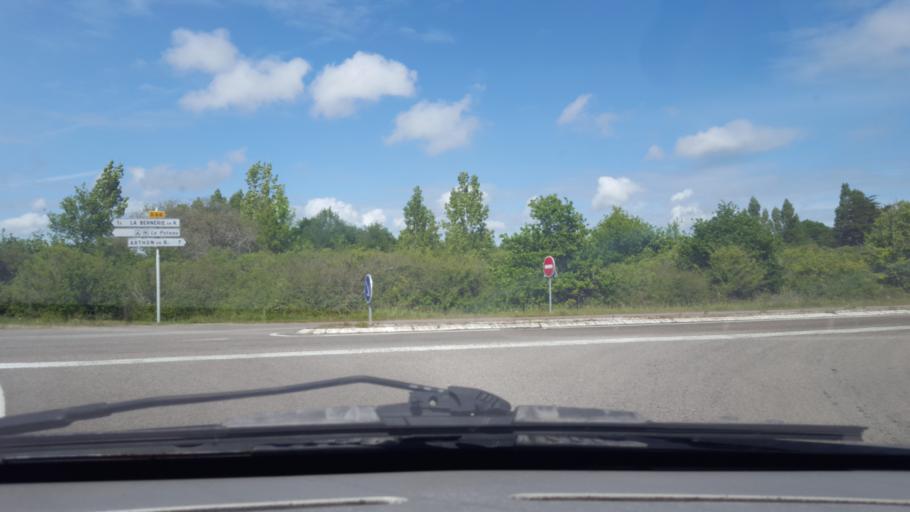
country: FR
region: Pays de la Loire
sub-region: Departement de la Loire-Atlantique
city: La Bernerie-en-Retz
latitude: 47.0884
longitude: -2.0256
